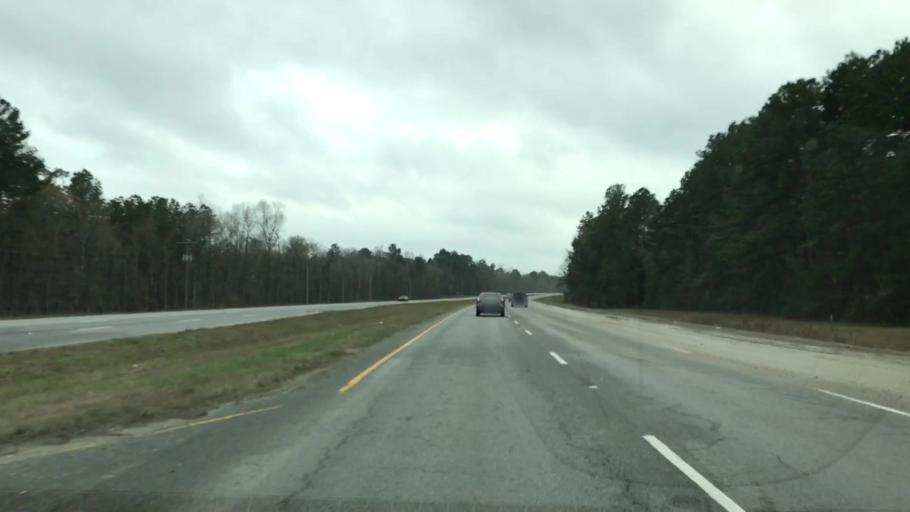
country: US
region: South Carolina
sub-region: Berkeley County
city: Moncks Corner
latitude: 33.1202
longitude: -80.0284
